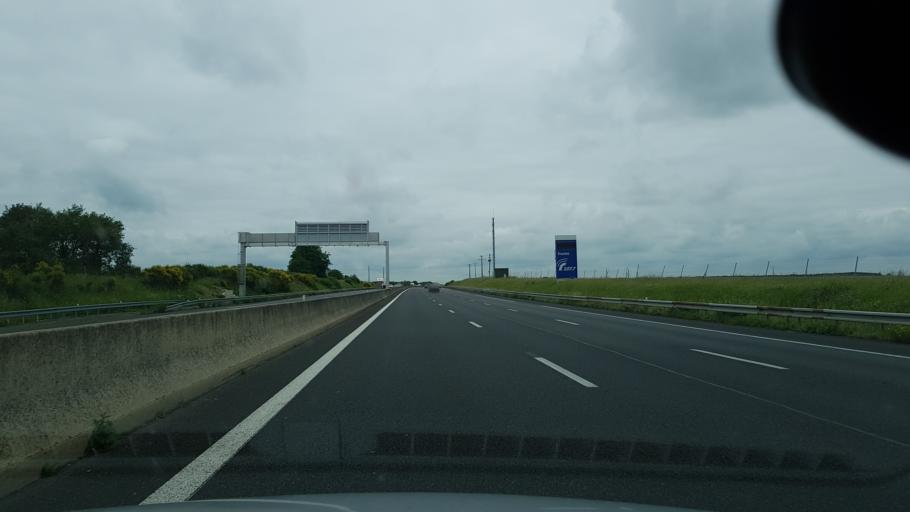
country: FR
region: Centre
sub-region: Departement du Loir-et-Cher
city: Villebarou
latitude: 47.6161
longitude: 1.2985
